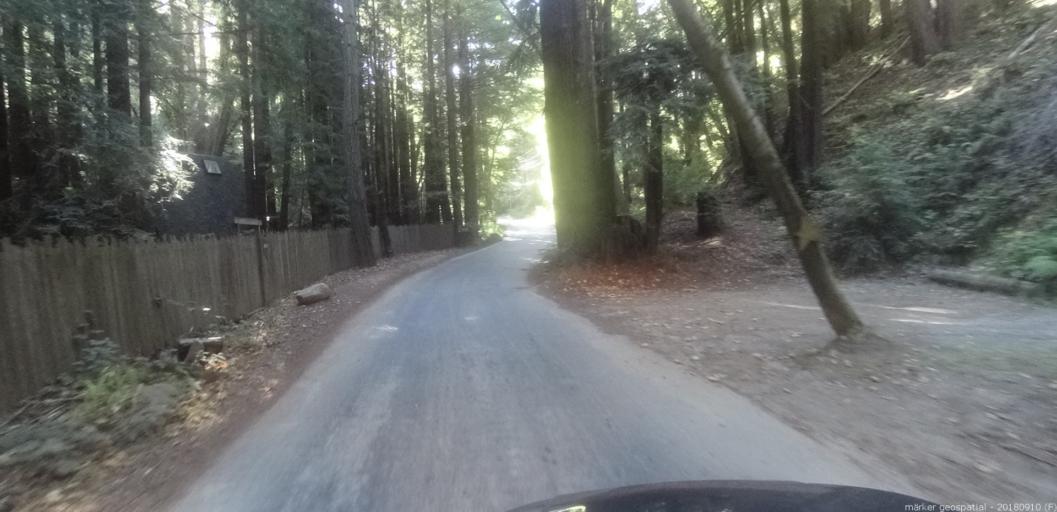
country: US
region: California
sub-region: Monterey County
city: Carmel Valley Village
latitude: 36.3925
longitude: -121.8772
